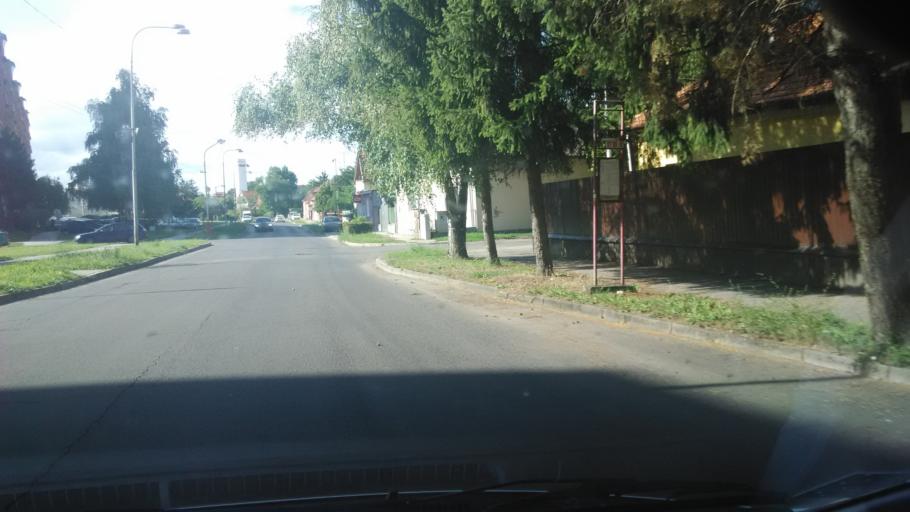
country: SK
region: Nitriansky
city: Levice
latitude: 48.2109
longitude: 18.6083
